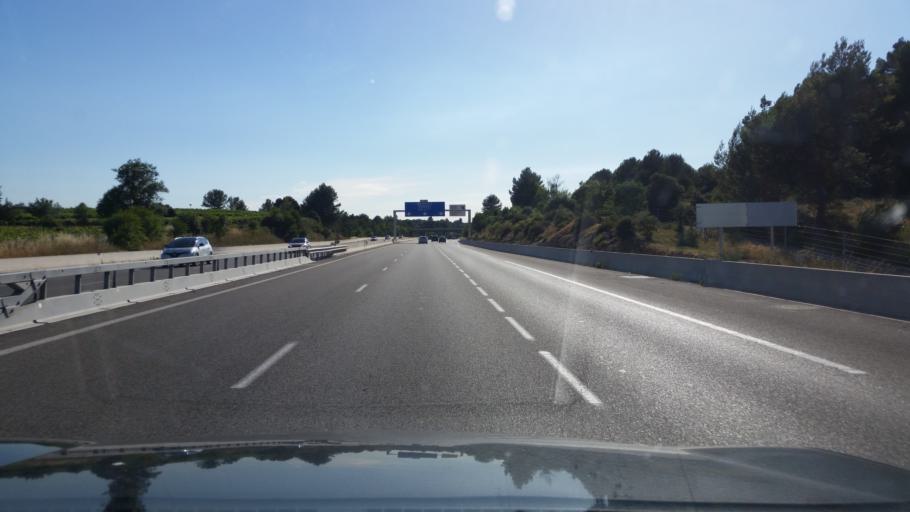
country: FR
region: Provence-Alpes-Cote d'Azur
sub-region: Departement du Var
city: Pourrieres
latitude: 43.4798
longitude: 5.7623
